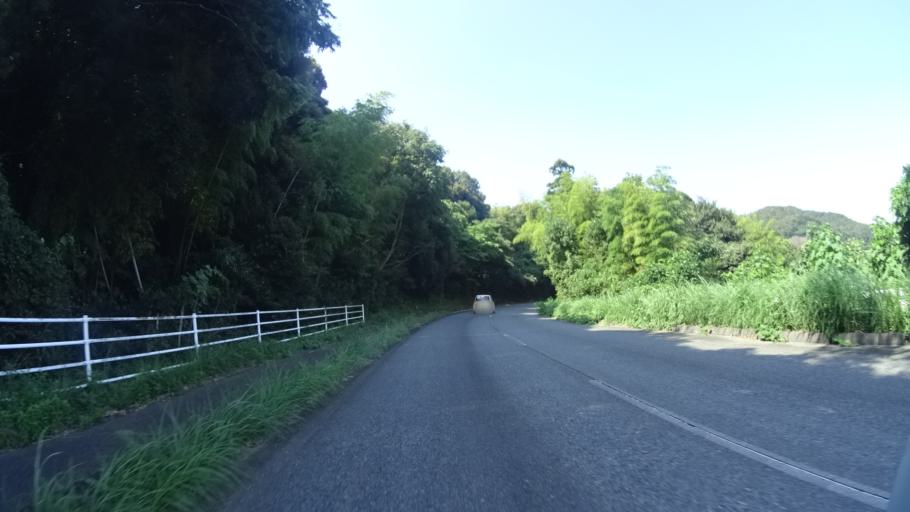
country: JP
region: Yamaguchi
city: Shimonoseki
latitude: 34.0932
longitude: 130.8855
